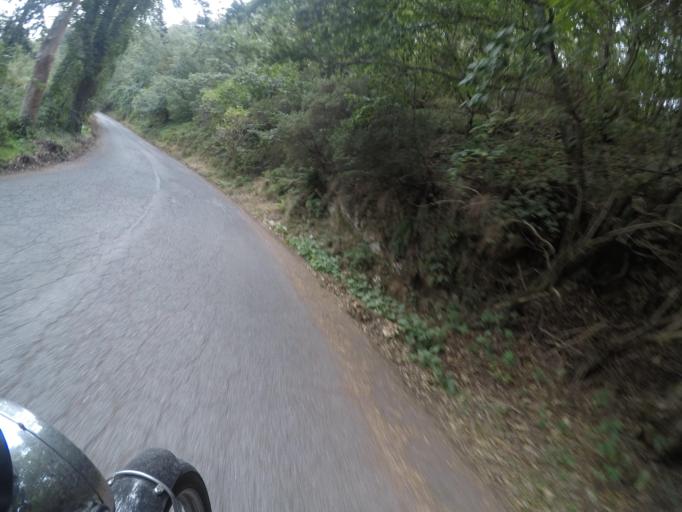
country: IT
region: Tuscany
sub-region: Provincia di Massa-Carrara
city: Fosdinovo
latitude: 44.1233
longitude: 10.0657
